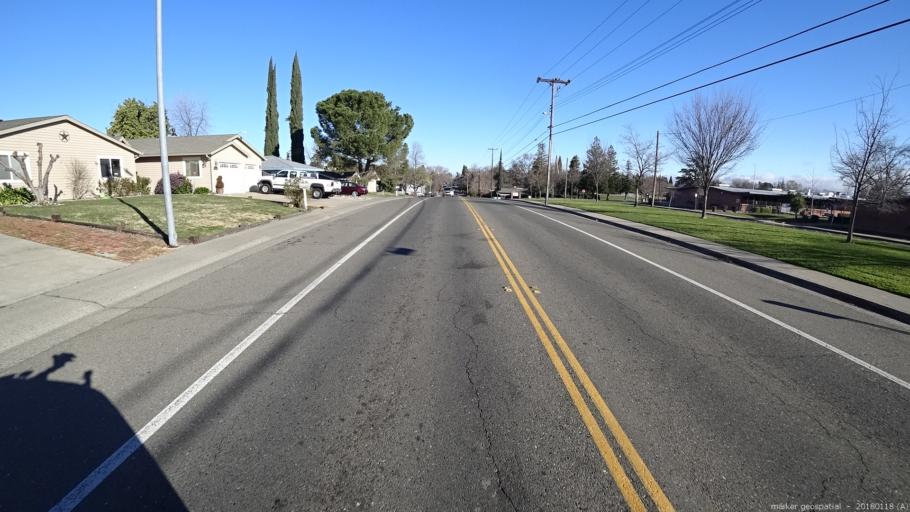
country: US
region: California
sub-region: Sacramento County
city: Orangevale
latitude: 38.6714
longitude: -121.2350
